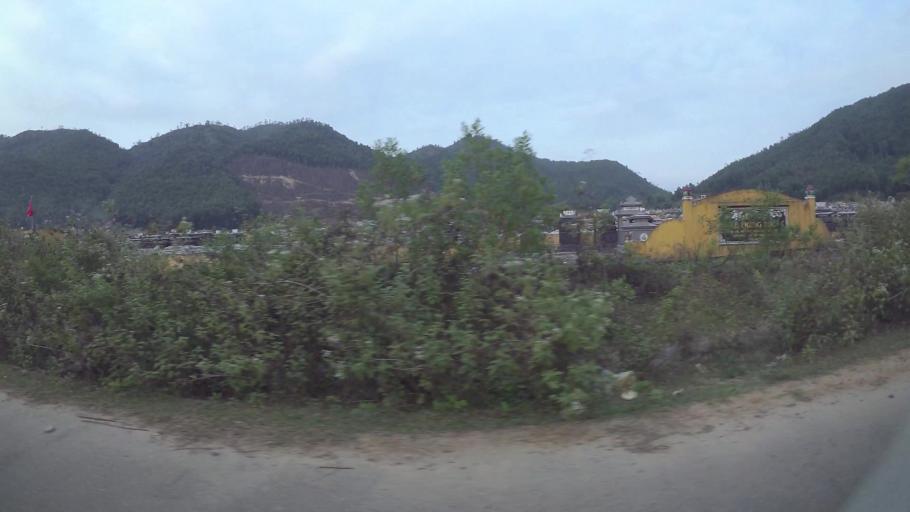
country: VN
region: Da Nang
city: Lien Chieu
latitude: 16.0580
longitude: 108.1246
